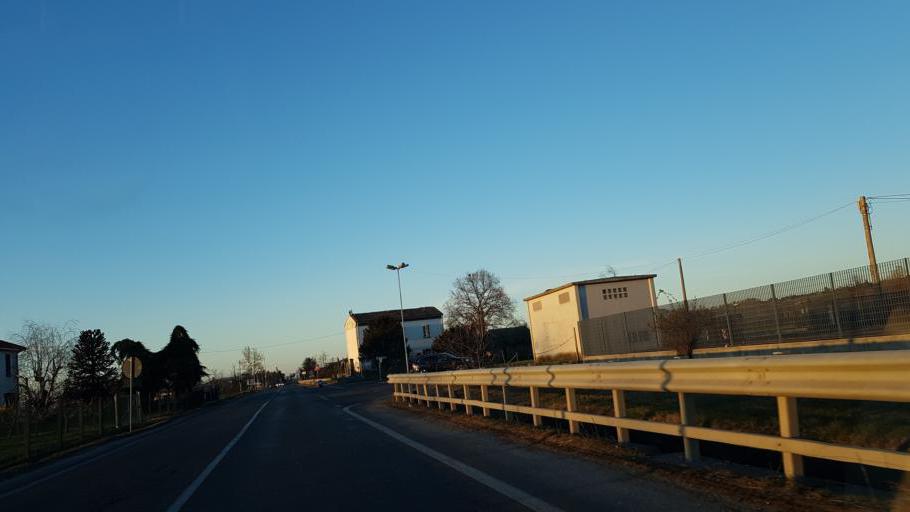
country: IT
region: Piedmont
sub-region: Provincia di Alessandria
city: Carbonara Scrivia
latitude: 44.8660
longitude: 8.8561
